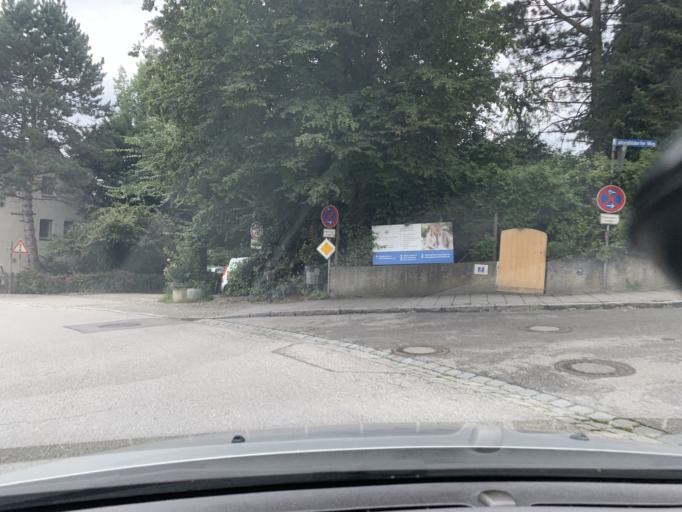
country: DE
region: Bavaria
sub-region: Upper Bavaria
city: Muehldorf
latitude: 48.2437
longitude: 12.5187
